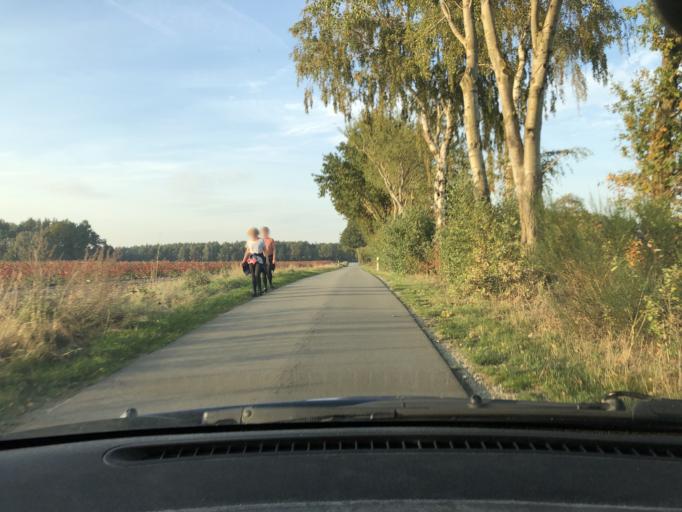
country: DE
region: Lower Saxony
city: Hitzacker
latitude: 53.1357
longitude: 11.0082
